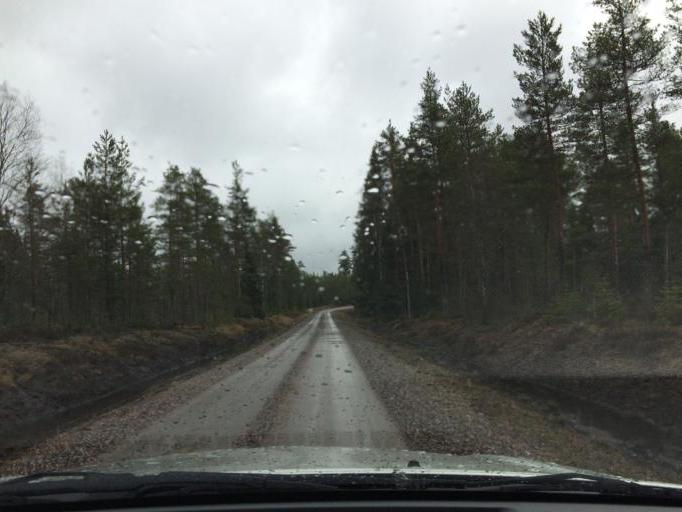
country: SE
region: OErebro
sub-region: Hallefors Kommun
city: Haellefors
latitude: 60.0290
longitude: 14.5552
